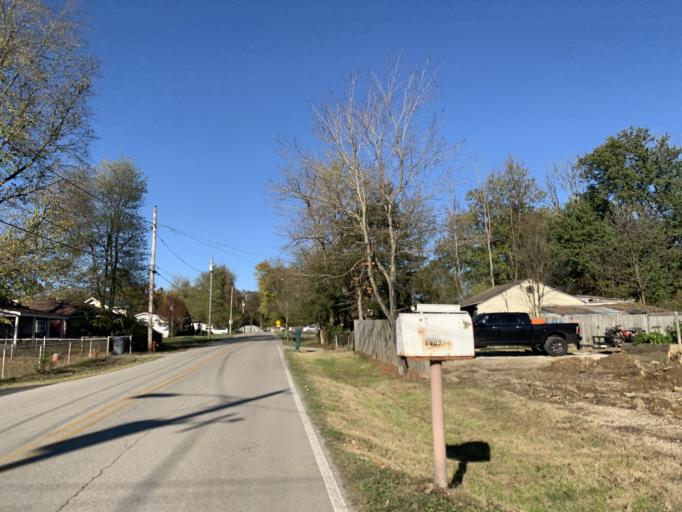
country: US
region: Kentucky
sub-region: Jefferson County
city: Pleasure Ridge Park
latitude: 38.1558
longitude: -85.8769
